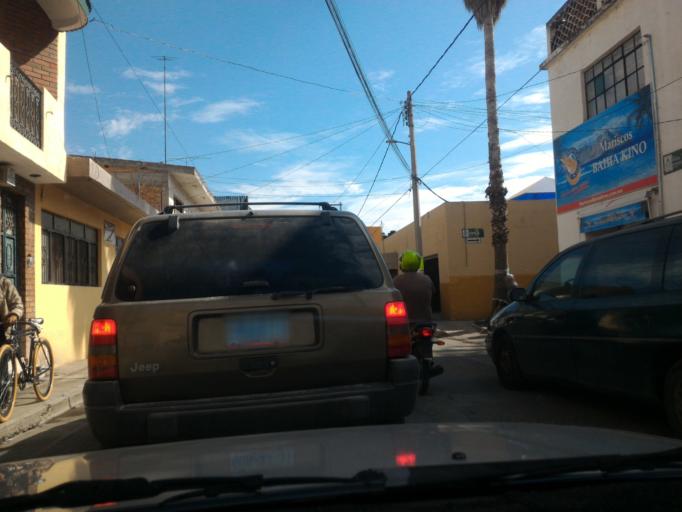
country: MX
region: Guanajuato
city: Ciudad Manuel Doblado
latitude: 20.7295
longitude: -101.9531
